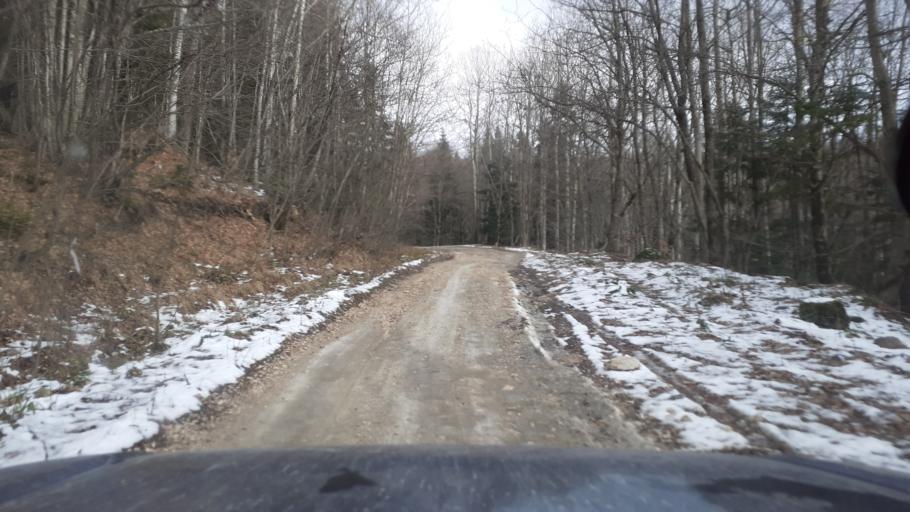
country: RU
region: Krasnodarskiy
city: Neftegorsk
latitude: 44.0734
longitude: 39.7592
